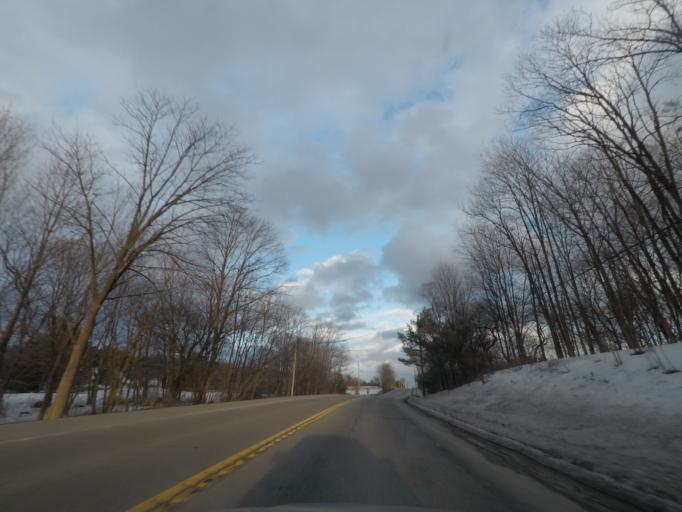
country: US
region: New York
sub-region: Montgomery County
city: Saint Johnsville
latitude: 43.0053
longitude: -74.7275
